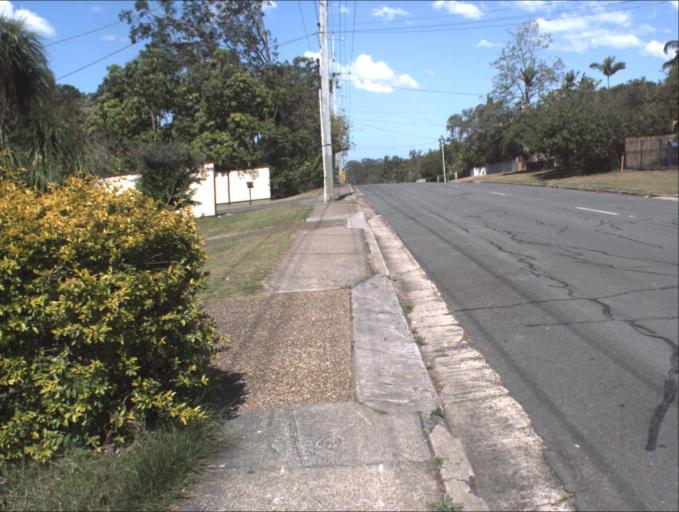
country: AU
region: Queensland
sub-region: Logan
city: Logan City
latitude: -27.6612
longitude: 153.1140
